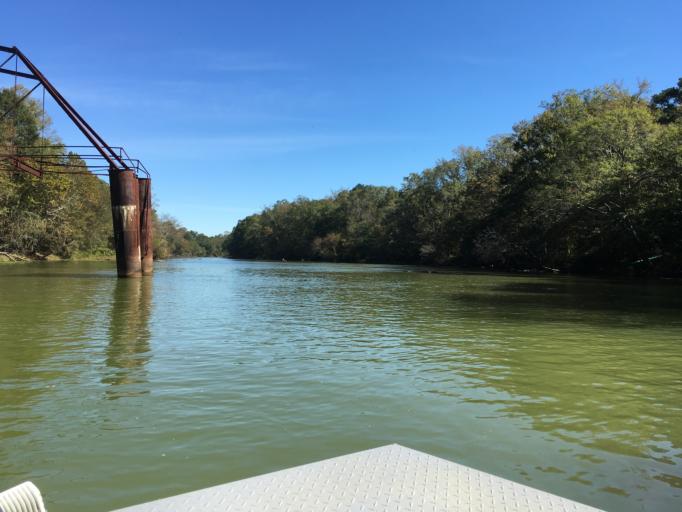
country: US
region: Georgia
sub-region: Fulton County
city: Johns Creek
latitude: 34.0012
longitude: -84.2347
